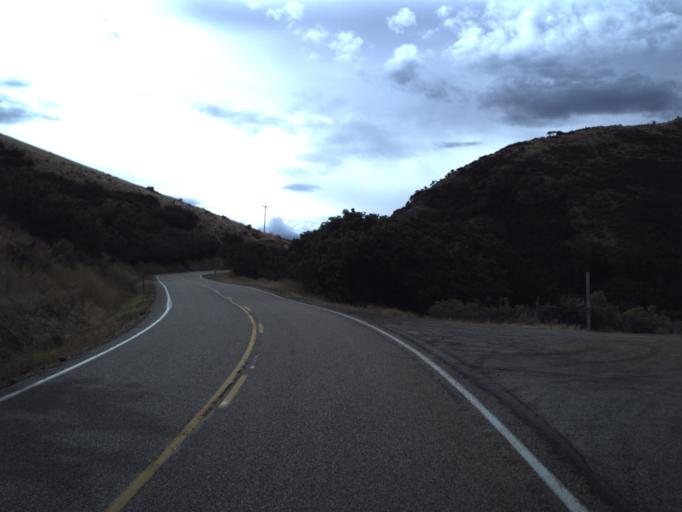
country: US
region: Utah
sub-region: Morgan County
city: Morgan
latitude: 40.9239
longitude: -111.6045
